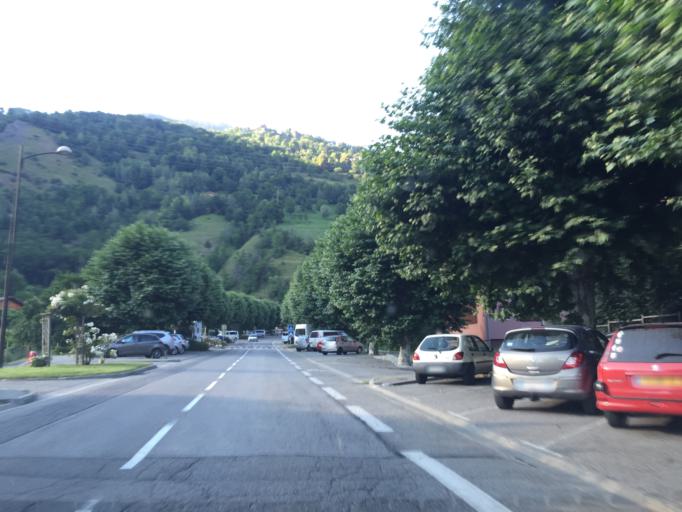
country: FR
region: Rhone-Alpes
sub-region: Departement de la Savoie
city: Bourg-Saint-Maurice
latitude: 45.6208
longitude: 6.7709
